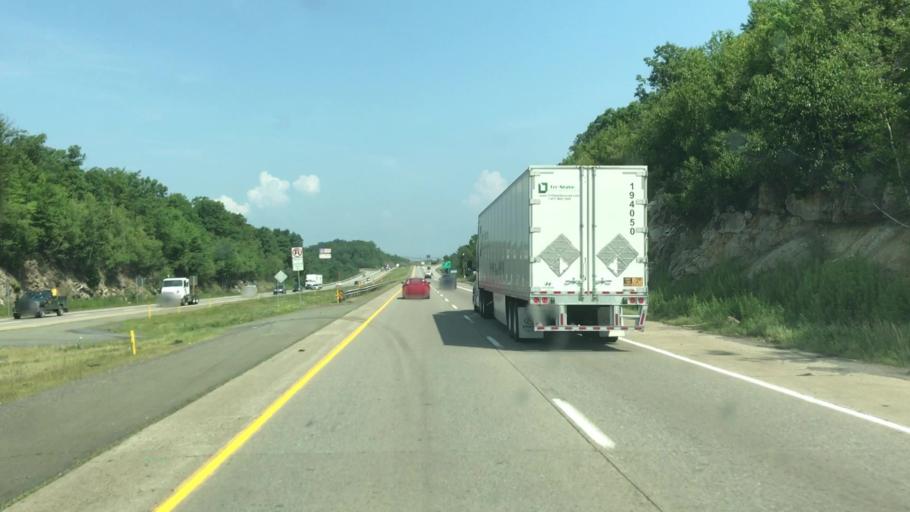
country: US
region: Pennsylvania
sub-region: Luzerne County
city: Conyngham
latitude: 40.9716
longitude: -76.0314
